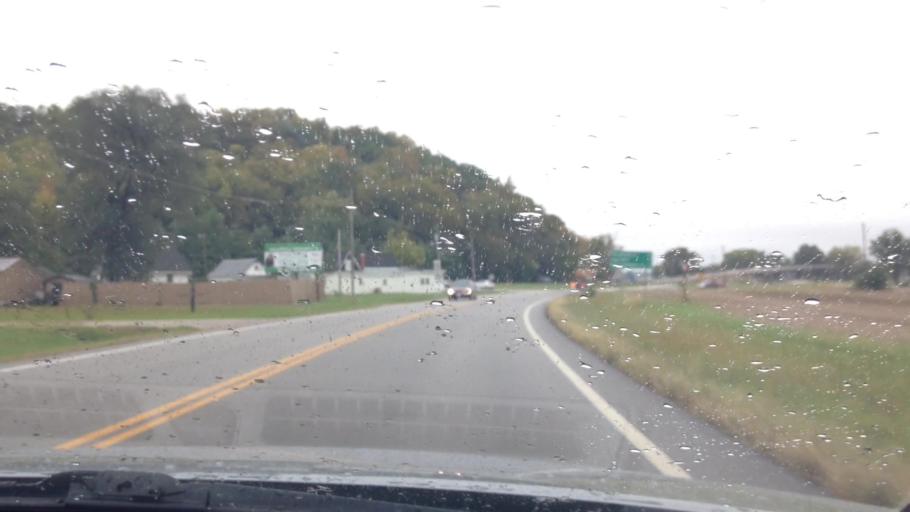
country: US
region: Missouri
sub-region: Platte County
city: Weston
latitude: 39.3696
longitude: -94.8664
